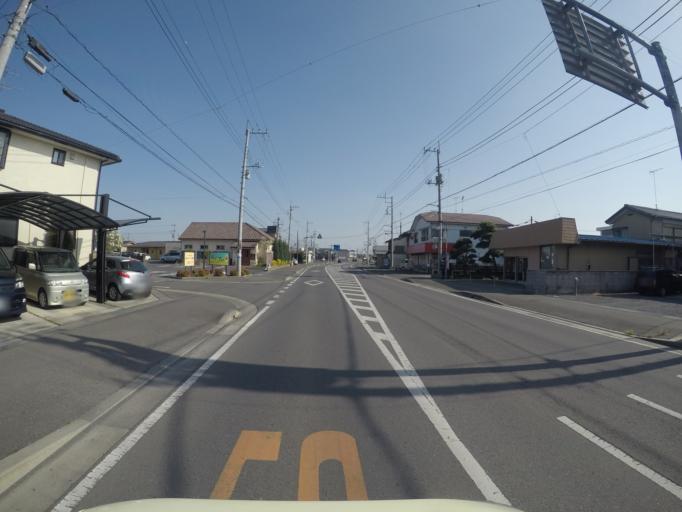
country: JP
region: Ibaraki
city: Yuki
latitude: 36.2961
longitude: 139.8769
